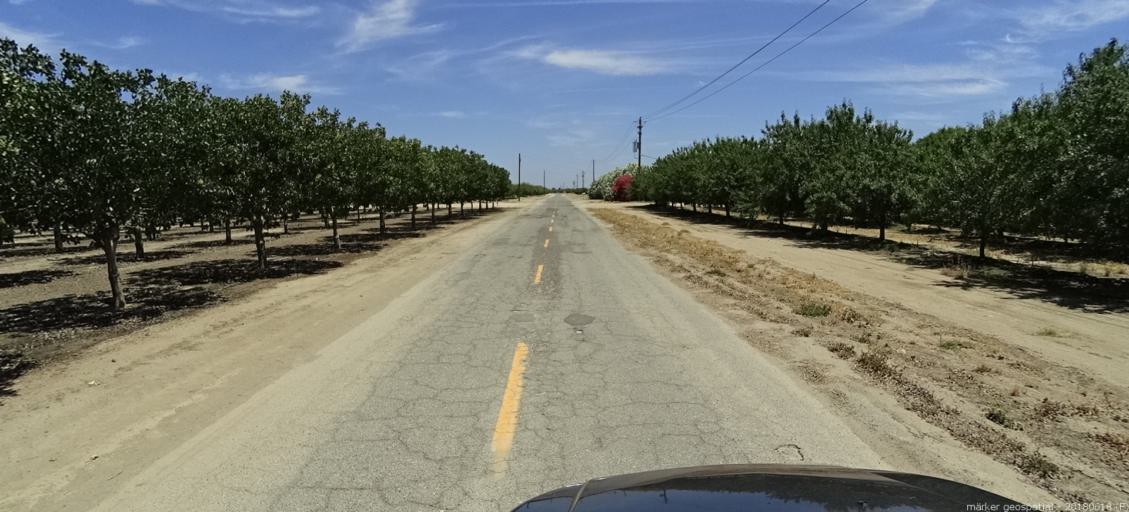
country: US
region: California
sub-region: Madera County
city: Parkwood
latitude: 36.9311
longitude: -120.0796
